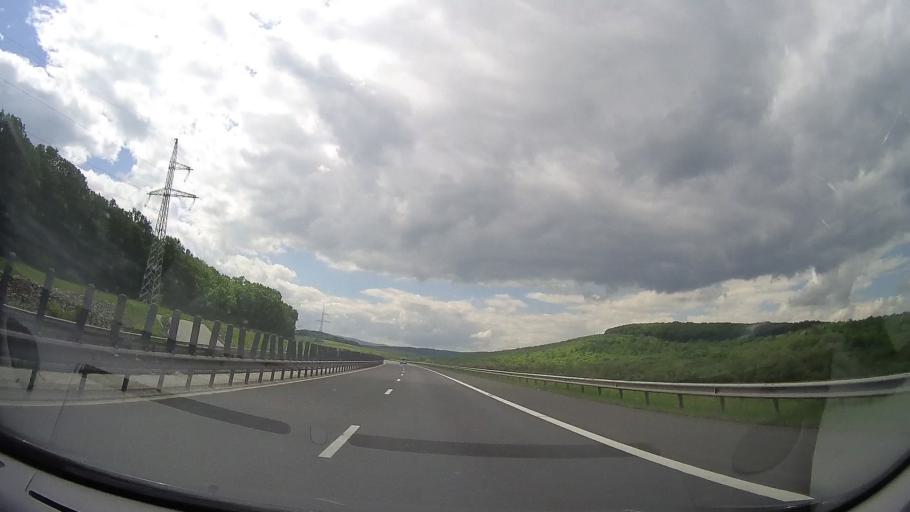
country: RO
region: Sibiu
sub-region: Comuna Cristian
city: Cristian
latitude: 45.8019
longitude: 24.0398
